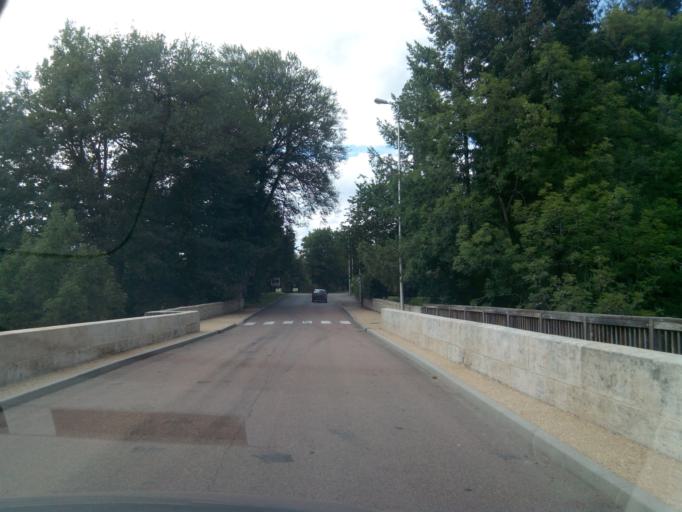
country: FR
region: Limousin
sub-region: Departement de la Haute-Vienne
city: Eymoutiers
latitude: 45.7390
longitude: 1.7388
